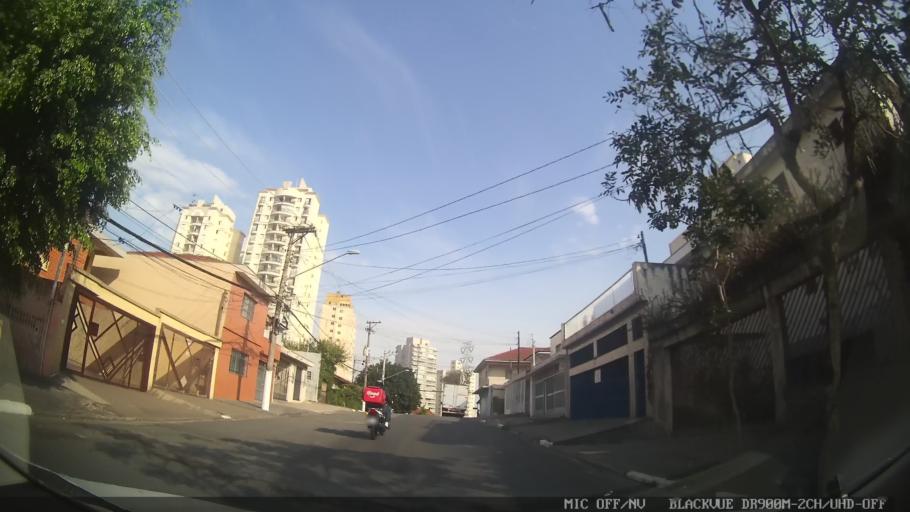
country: BR
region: Sao Paulo
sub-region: Sao Caetano Do Sul
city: Sao Caetano do Sul
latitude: -23.6015
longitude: -46.6071
